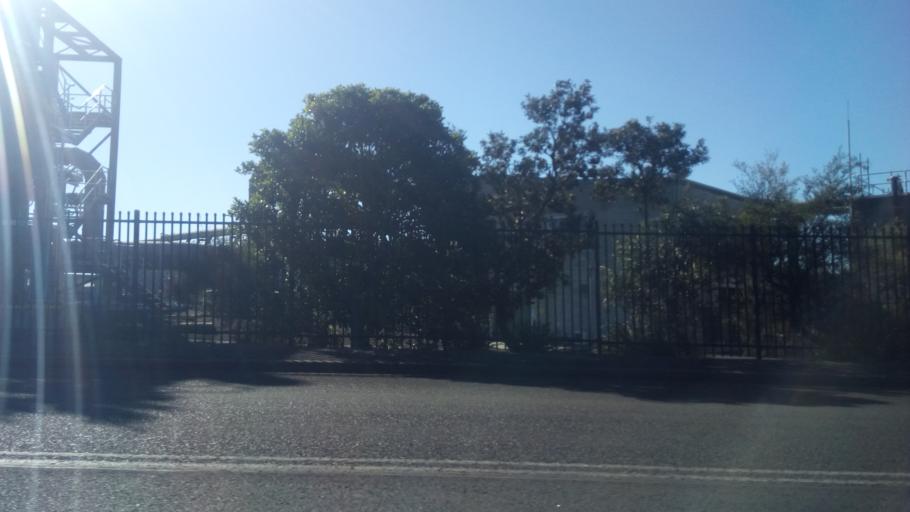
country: AU
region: New South Wales
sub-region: Wollongong
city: Coniston
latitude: -34.4448
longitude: 150.8979
